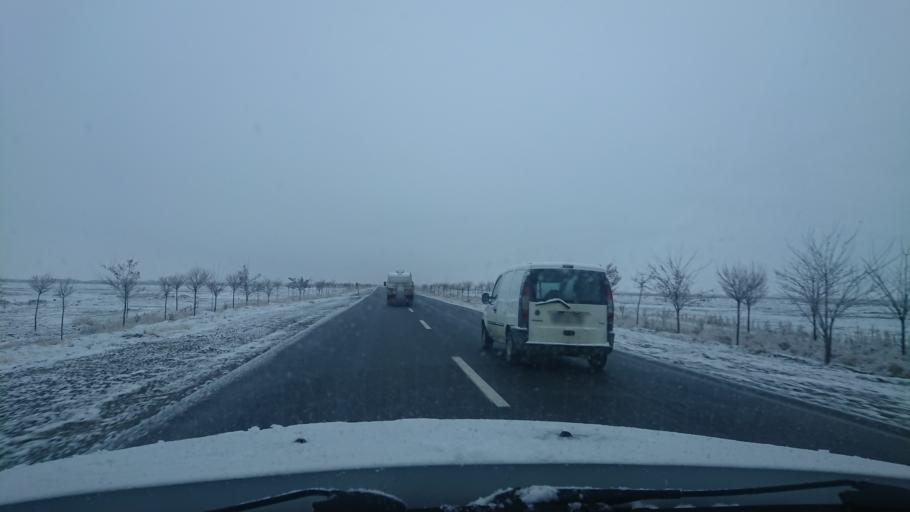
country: TR
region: Aksaray
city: Yesilova
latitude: 38.3125
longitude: 33.7537
